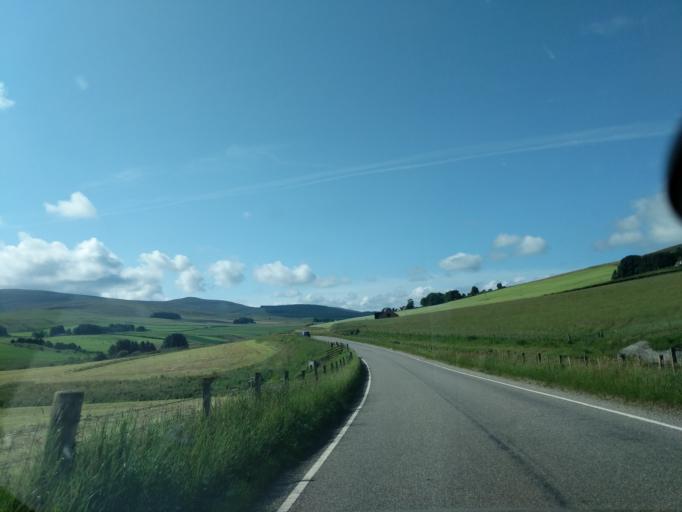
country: GB
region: Scotland
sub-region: Moray
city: Dufftown
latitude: 57.3863
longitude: -3.2188
